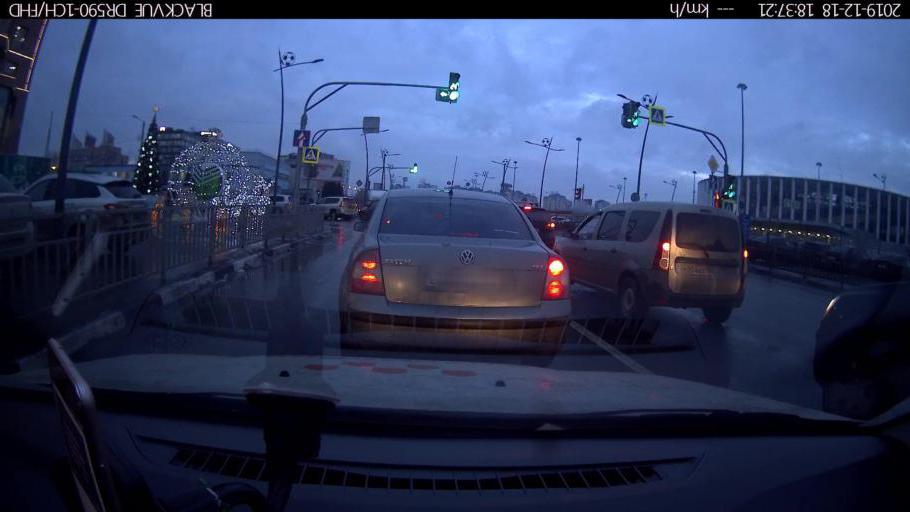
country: RU
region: Nizjnij Novgorod
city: Nizhniy Novgorod
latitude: 56.2703
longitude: 43.9870
